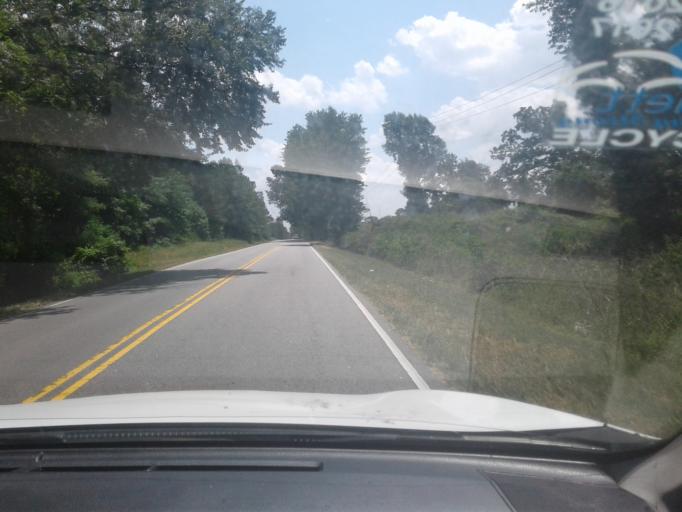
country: US
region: North Carolina
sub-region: Johnston County
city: Benson
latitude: 35.4139
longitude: -78.5401
